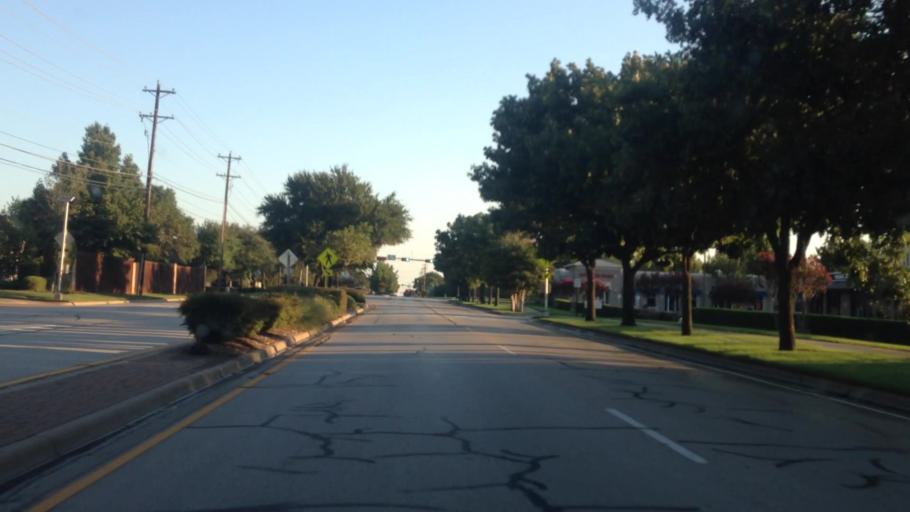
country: US
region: Texas
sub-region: Tarrant County
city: Southlake
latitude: 32.9441
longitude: -97.1341
